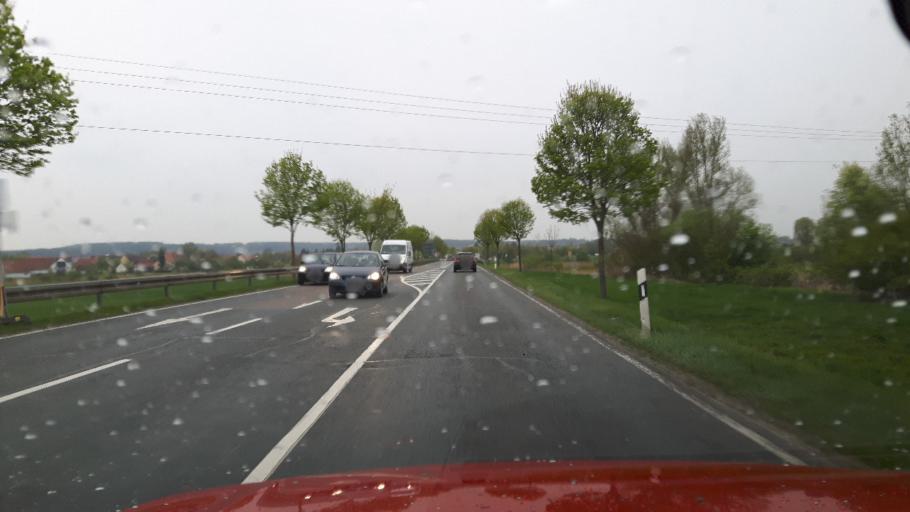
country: DE
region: Bavaria
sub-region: Regierungsbezirk Mittelfranken
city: Gunzenhausen
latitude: 49.1012
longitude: 10.7570
